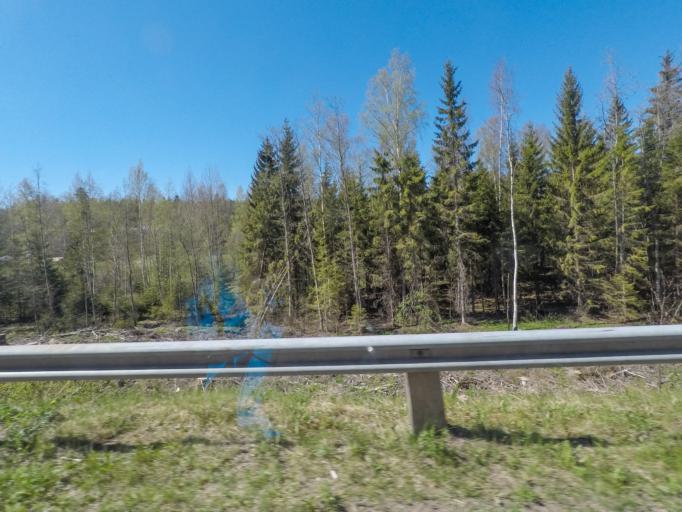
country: FI
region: Uusimaa
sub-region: Helsinki
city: Sammatti
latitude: 60.4084
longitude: 23.8203
